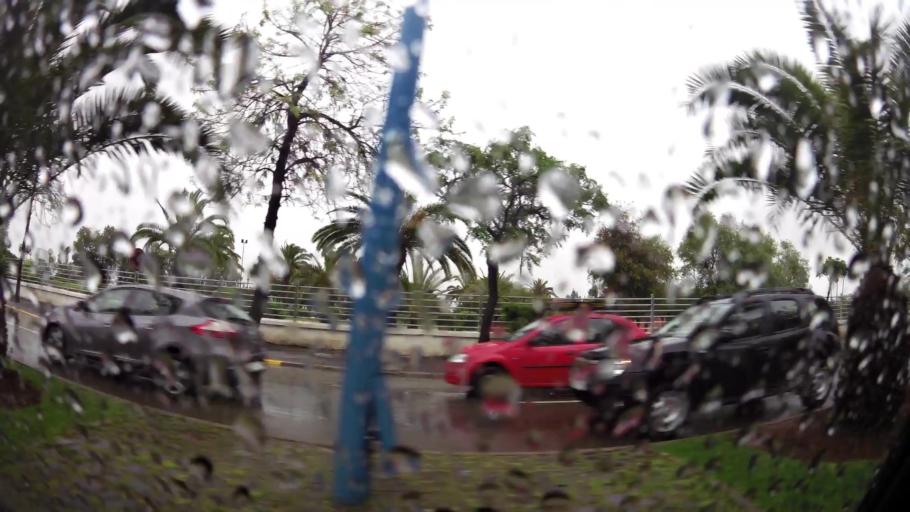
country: MA
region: Grand Casablanca
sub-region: Casablanca
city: Casablanca
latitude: 33.5610
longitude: -7.6694
